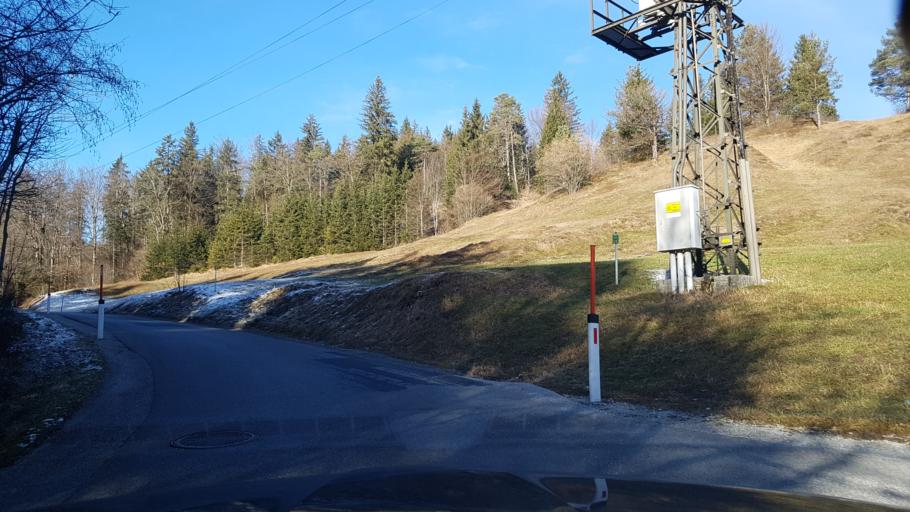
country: AT
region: Salzburg
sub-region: Politischer Bezirk Salzburg-Umgebung
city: Ebenau
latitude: 47.7666
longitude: 13.1772
